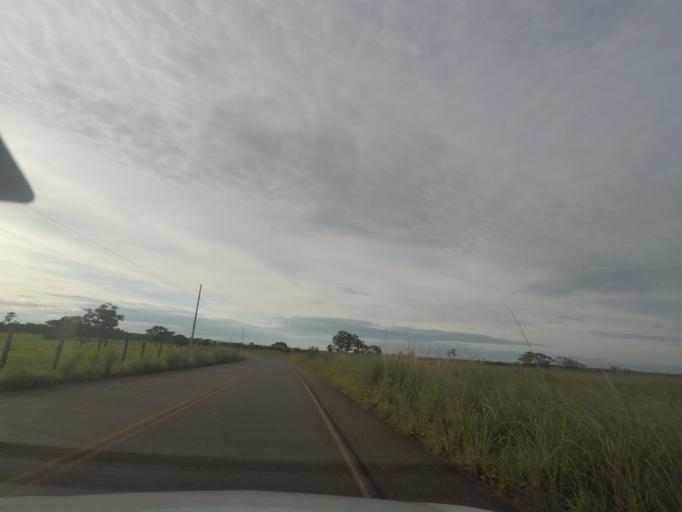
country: BR
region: Goias
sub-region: Trindade
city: Trindade
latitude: -16.7299
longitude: -49.4247
